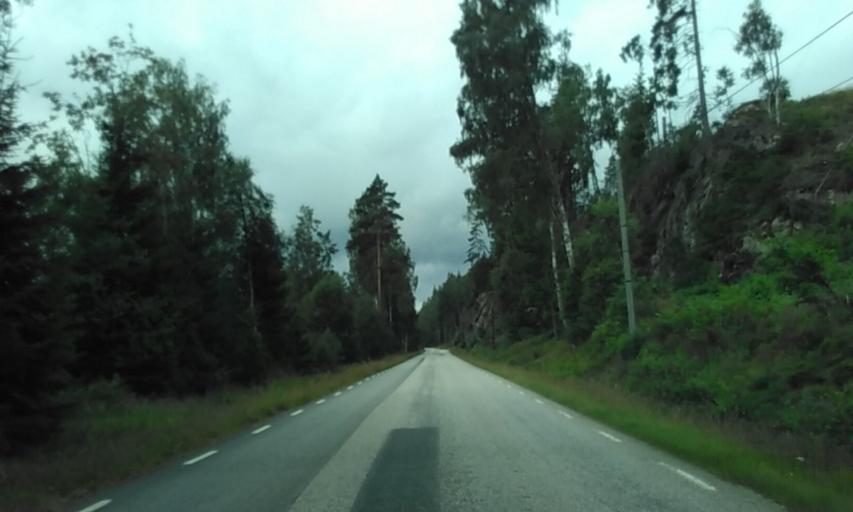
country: SE
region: Vaestra Goetaland
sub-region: Bollebygds Kommun
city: Bollebygd
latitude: 57.7562
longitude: 12.6259
